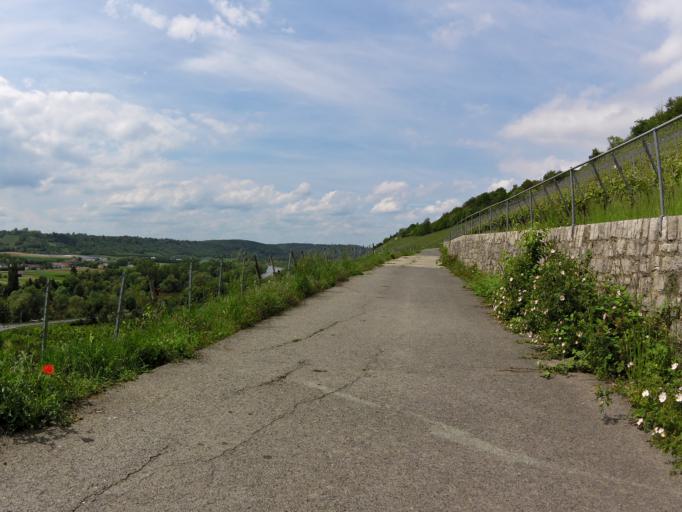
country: DE
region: Bavaria
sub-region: Regierungsbezirk Unterfranken
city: Sommerhausen
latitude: 49.7106
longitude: 10.0237
